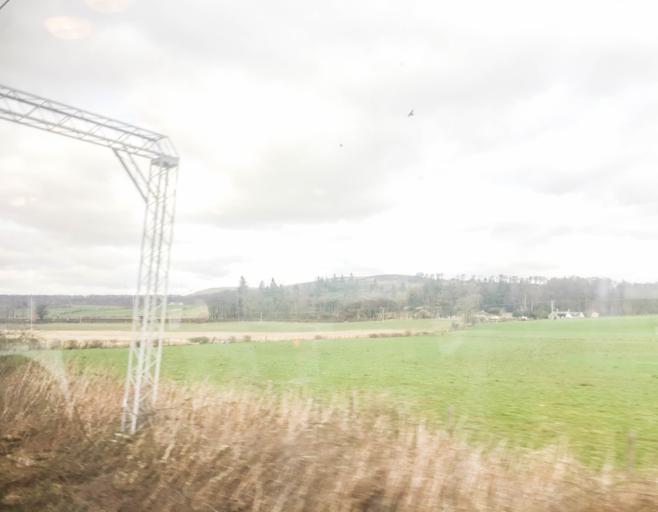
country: GB
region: Scotland
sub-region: Inverclyde
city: Port Glasgow
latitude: 55.9771
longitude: -4.6853
